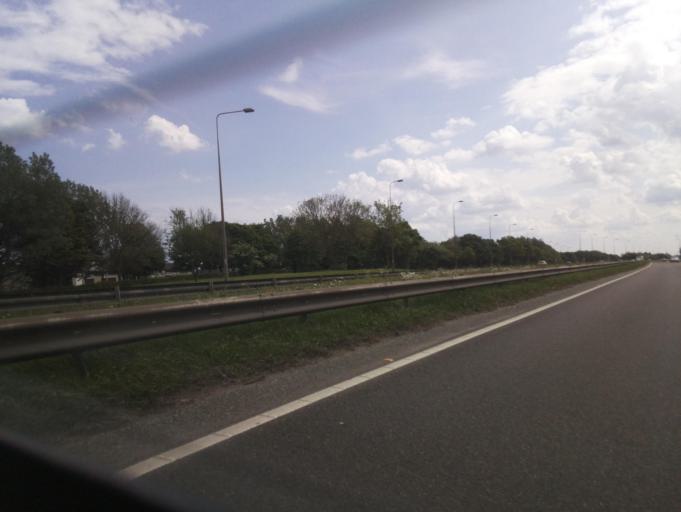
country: GB
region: England
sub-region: County Durham
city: Shotton
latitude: 54.7694
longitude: -1.3573
